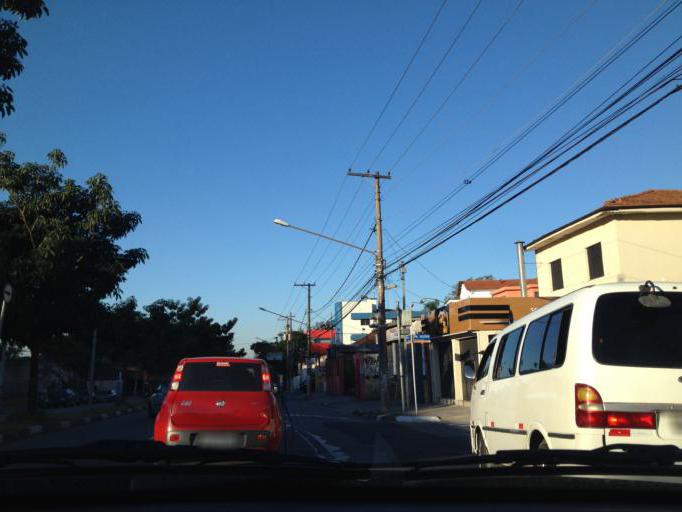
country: BR
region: Sao Paulo
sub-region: Osasco
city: Osasco
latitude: -23.5713
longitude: -46.7200
